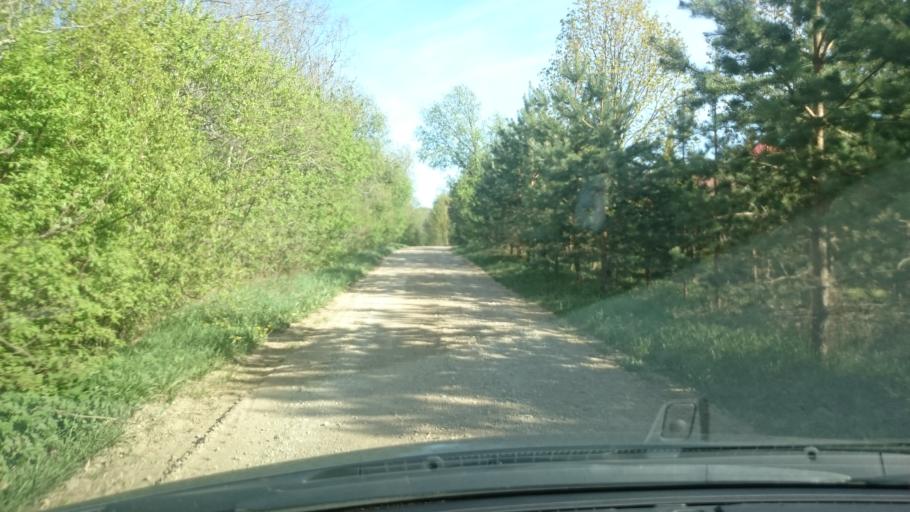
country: EE
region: Laeaene-Virumaa
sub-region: Kadrina vald
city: Kadrina
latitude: 59.3240
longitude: 26.0967
